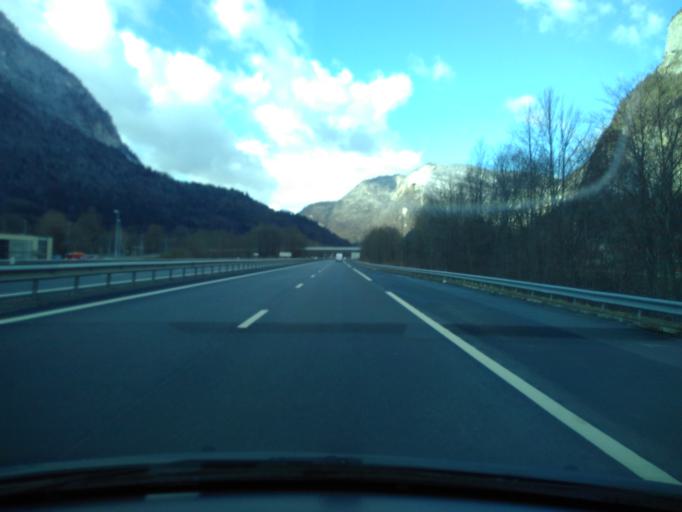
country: FR
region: Rhone-Alpes
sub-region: Departement de la Haute-Savoie
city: Magland
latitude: 46.0173
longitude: 6.6207
